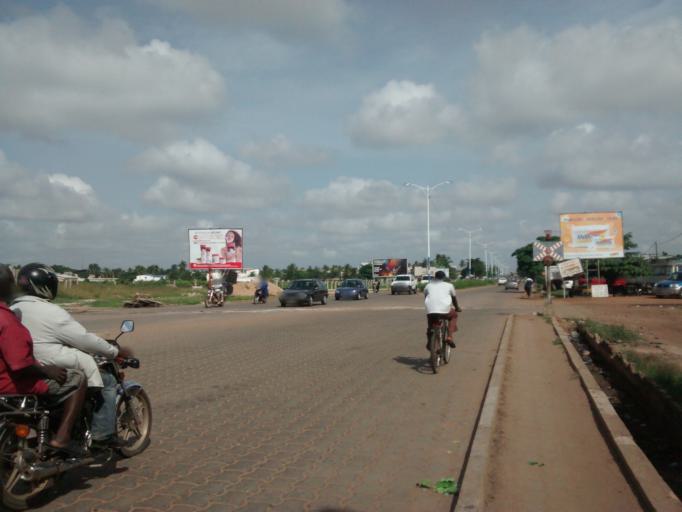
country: TG
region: Maritime
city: Lome
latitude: 6.1949
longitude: 1.2063
